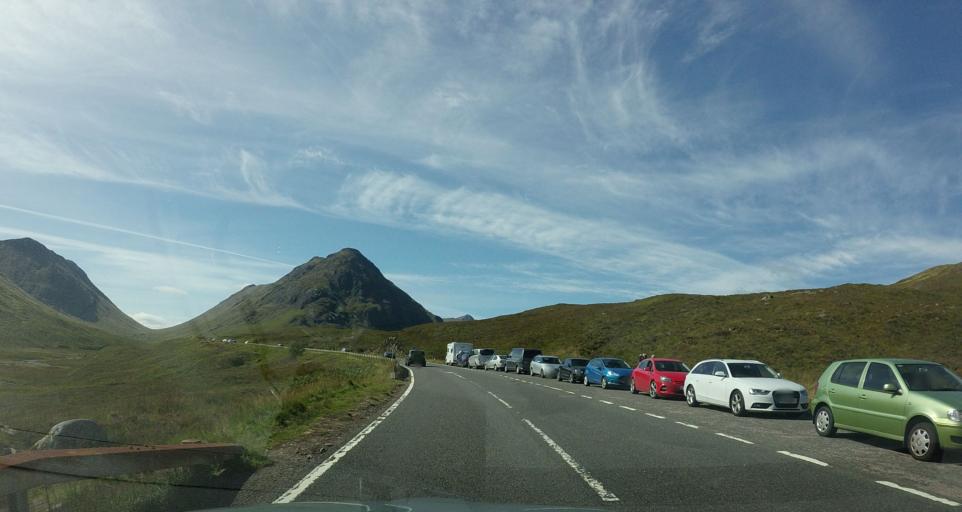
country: GB
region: Scotland
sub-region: Highland
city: Spean Bridge
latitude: 56.6650
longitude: -4.9062
